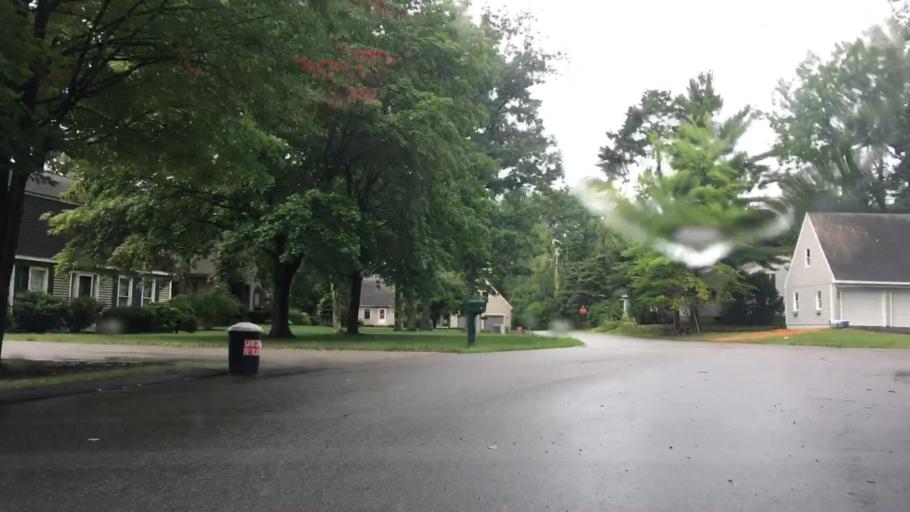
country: US
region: Maine
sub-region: York County
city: South Sanford
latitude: 43.4202
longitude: -70.7623
